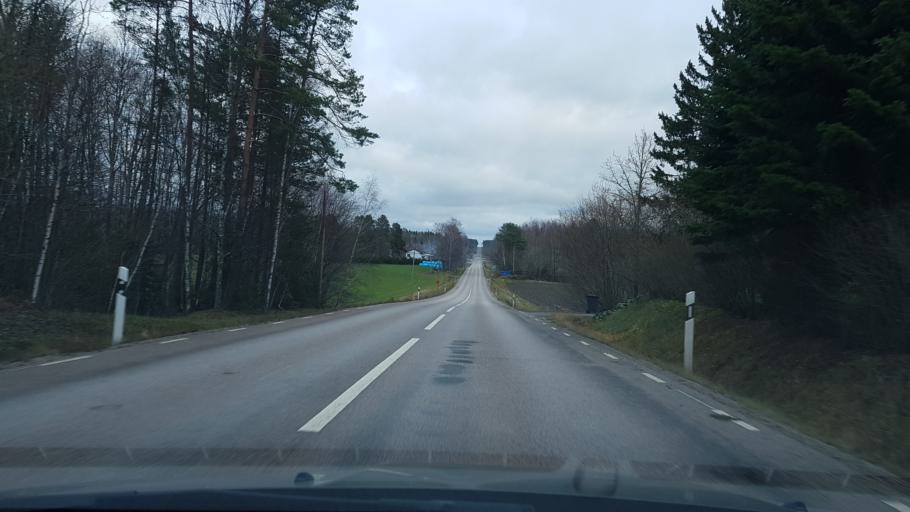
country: SE
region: Stockholm
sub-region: Norrtalje Kommun
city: Nykvarn
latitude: 59.9878
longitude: 18.2579
